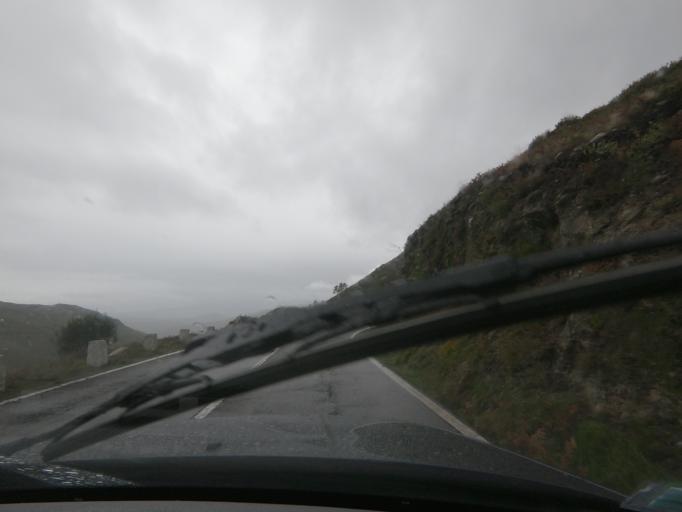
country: PT
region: Vila Real
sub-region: Mondim de Basto
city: Mondim de Basto
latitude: 41.3406
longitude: -7.8679
